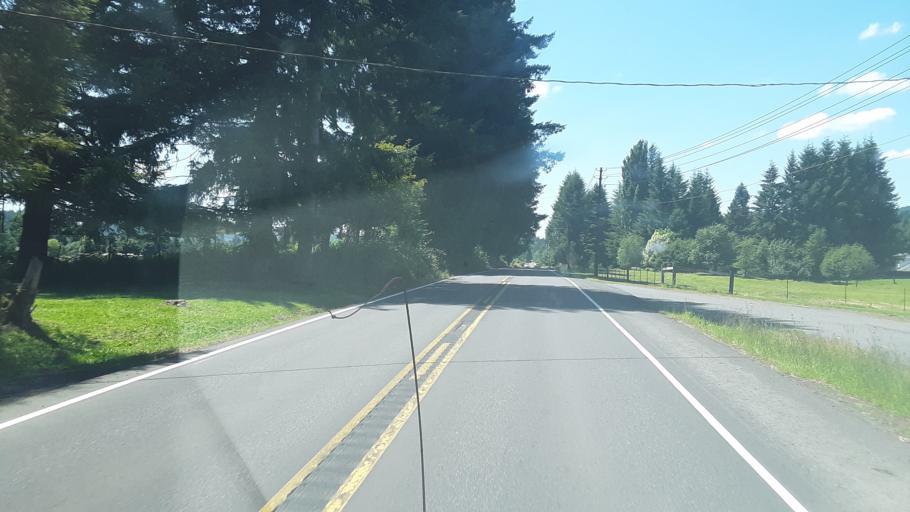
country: US
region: Washington
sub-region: Clark County
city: Amboy
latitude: 45.9243
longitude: -122.4023
